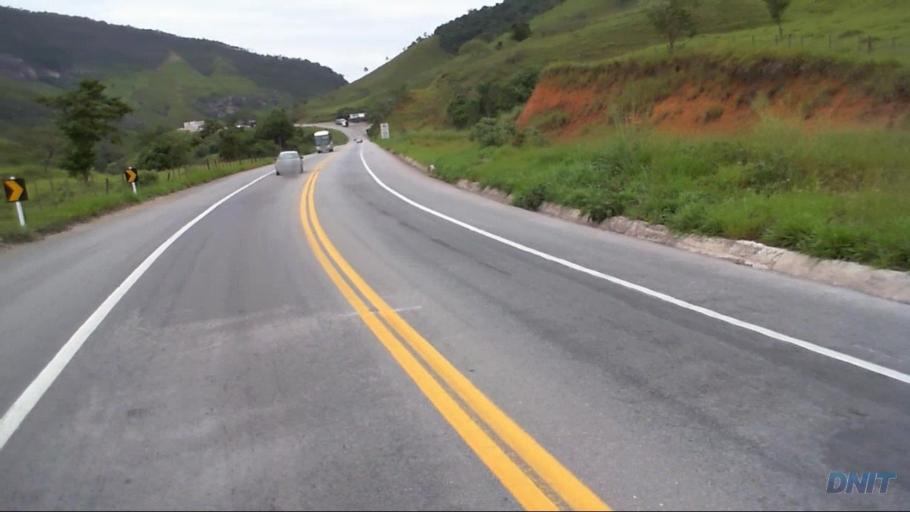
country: BR
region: Minas Gerais
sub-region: Timoteo
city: Timoteo
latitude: -19.6202
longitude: -42.8419
